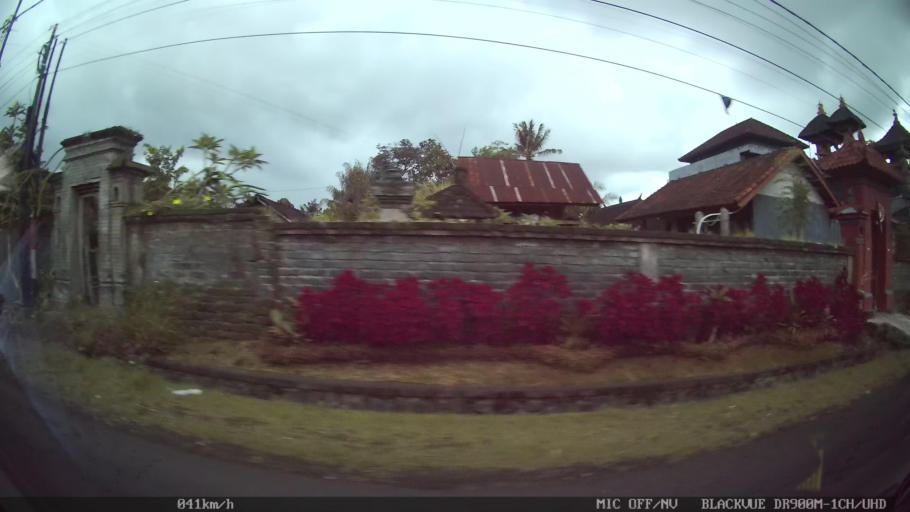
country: ID
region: Bali
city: Banjar Sempidi
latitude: -8.5234
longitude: 115.1906
